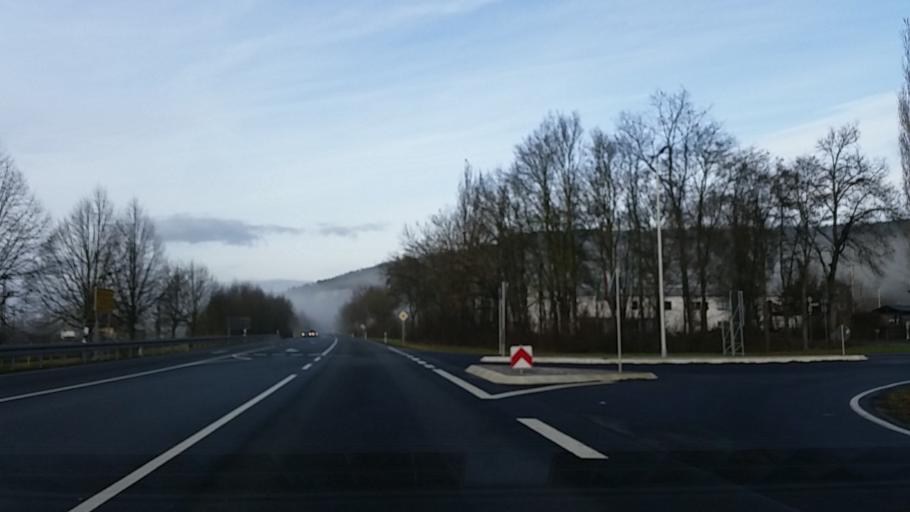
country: DE
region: Bavaria
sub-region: Regierungsbezirk Unterfranken
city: Thungersheim
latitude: 49.8825
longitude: 9.8389
